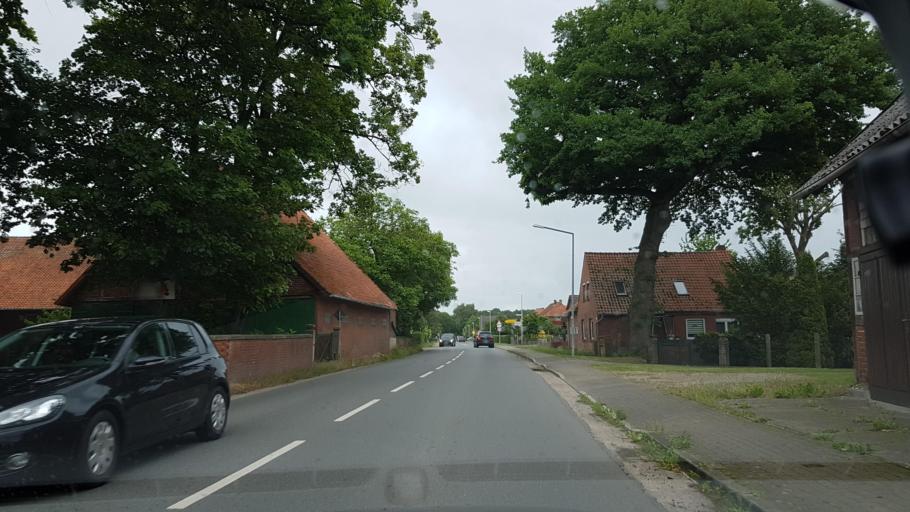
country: DE
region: Lower Saxony
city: Neustadt am Rubenberge
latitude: 52.5535
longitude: 9.5057
